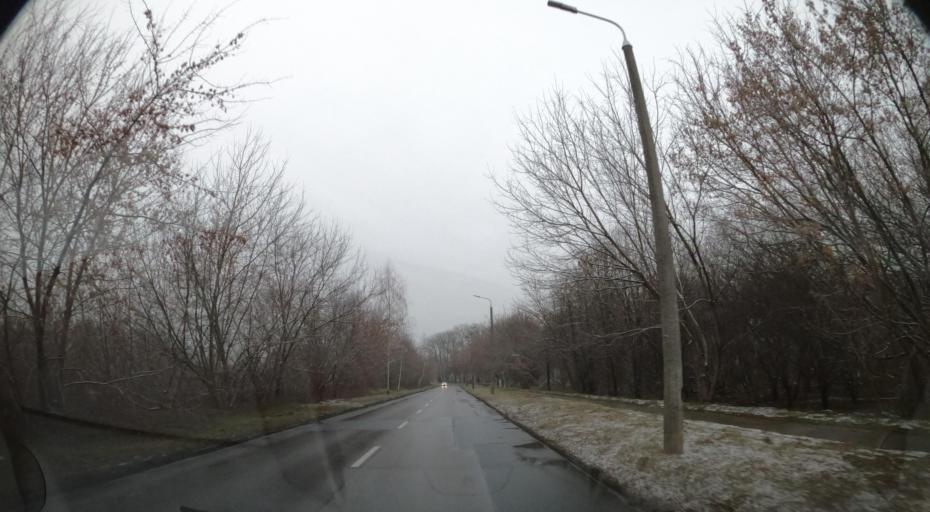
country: PL
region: Masovian Voivodeship
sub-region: Radom
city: Radom
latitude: 51.3857
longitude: 21.1190
